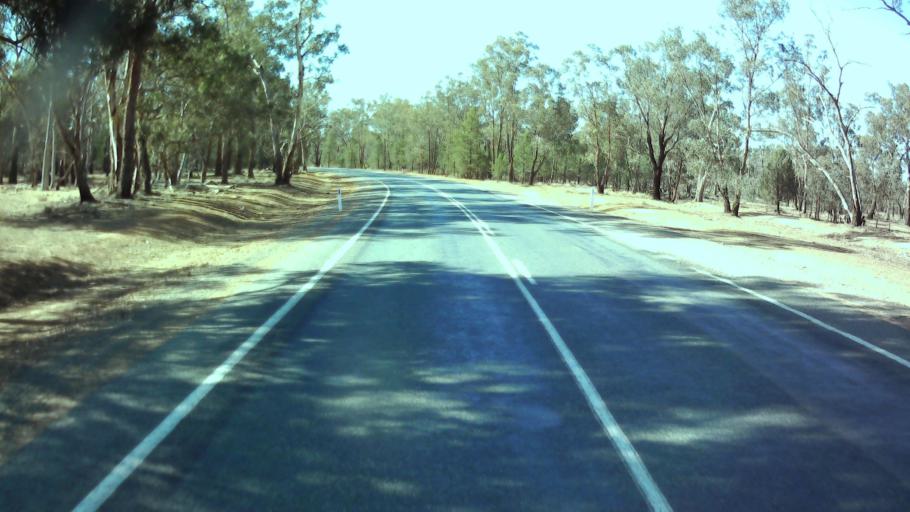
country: AU
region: New South Wales
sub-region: Weddin
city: Grenfell
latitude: -33.7296
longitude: 148.0888
